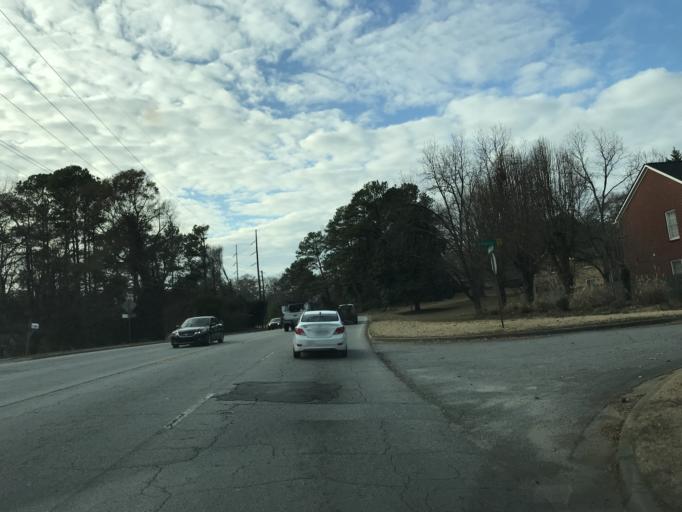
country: US
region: Georgia
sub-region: DeKalb County
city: Tucker
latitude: 33.8846
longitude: -84.2363
